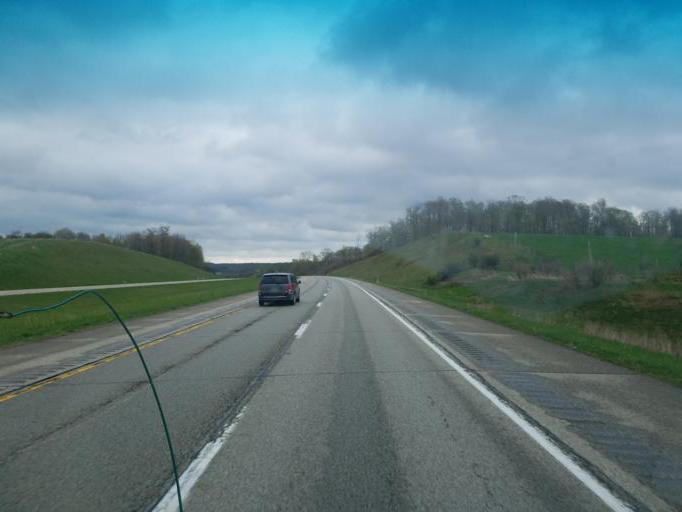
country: US
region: Pennsylvania
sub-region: Erie County
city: North East
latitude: 42.1244
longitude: -79.7923
